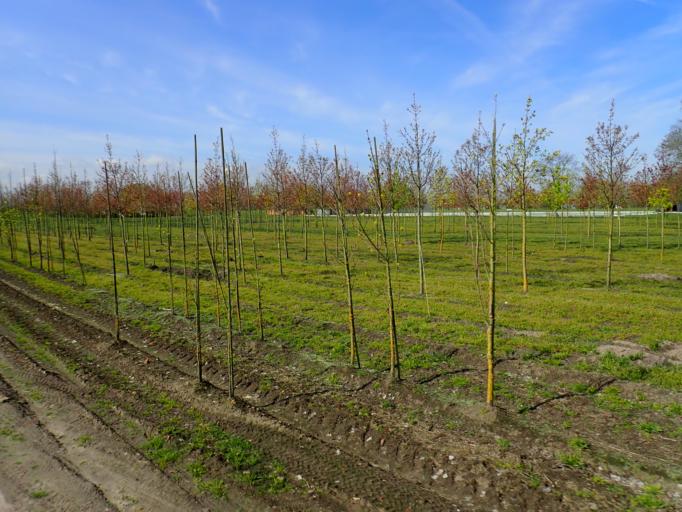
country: BE
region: Flanders
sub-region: Provincie Antwerpen
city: Putte
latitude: 51.0682
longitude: 4.6160
